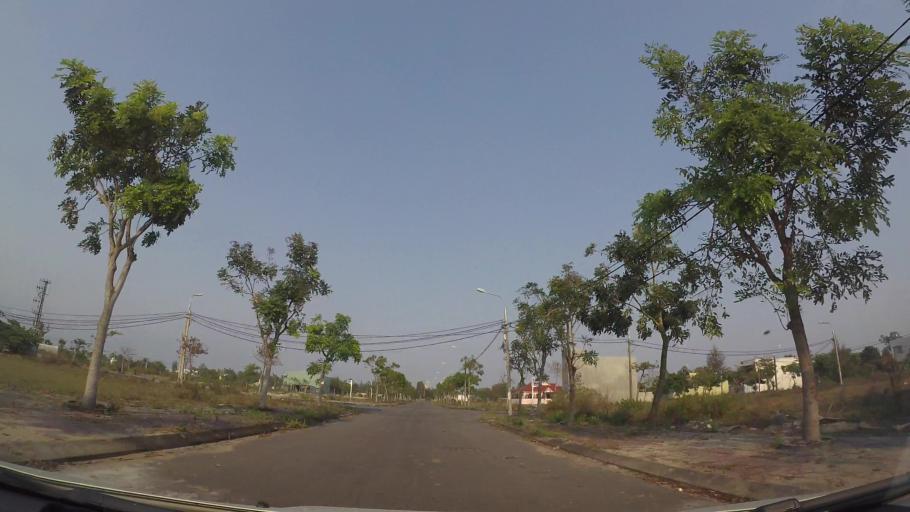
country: VN
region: Da Nang
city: Ngu Hanh Son
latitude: 15.9591
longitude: 108.2597
